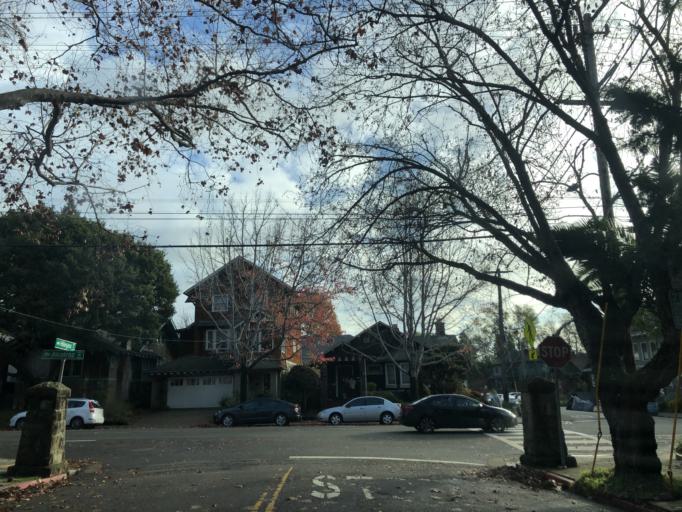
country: US
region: California
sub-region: Alameda County
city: Berkeley
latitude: 37.8513
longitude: -122.2546
